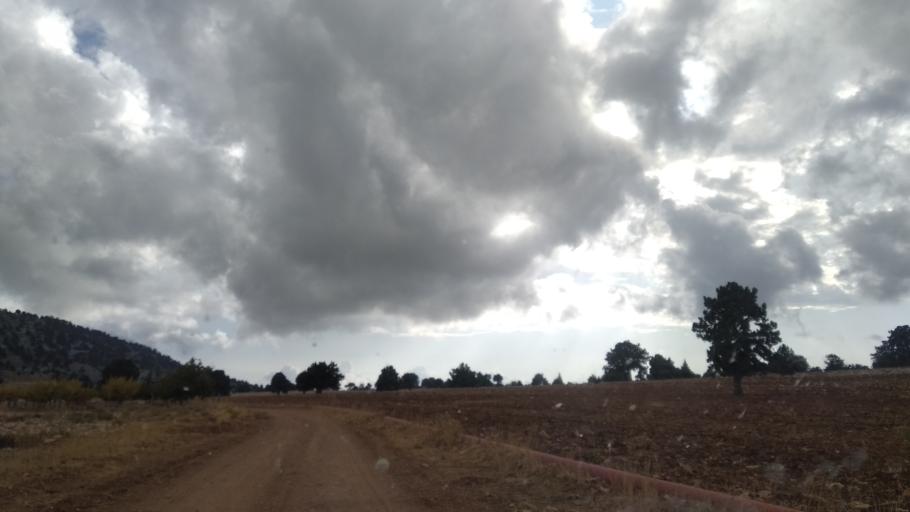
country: TR
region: Mersin
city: Sarikavak
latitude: 36.5644
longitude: 33.7378
